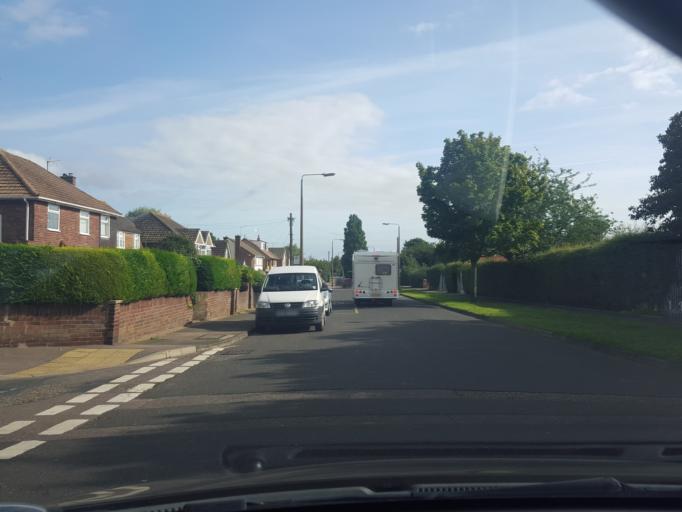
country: GB
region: England
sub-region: Essex
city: Dovercourt
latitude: 51.9289
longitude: 1.2632
